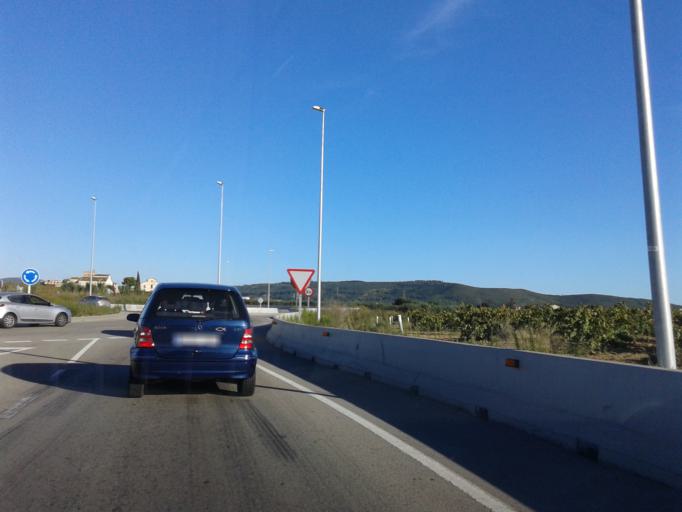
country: ES
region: Catalonia
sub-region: Provincia de Barcelona
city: La Granada
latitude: 41.3528
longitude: 1.7334
